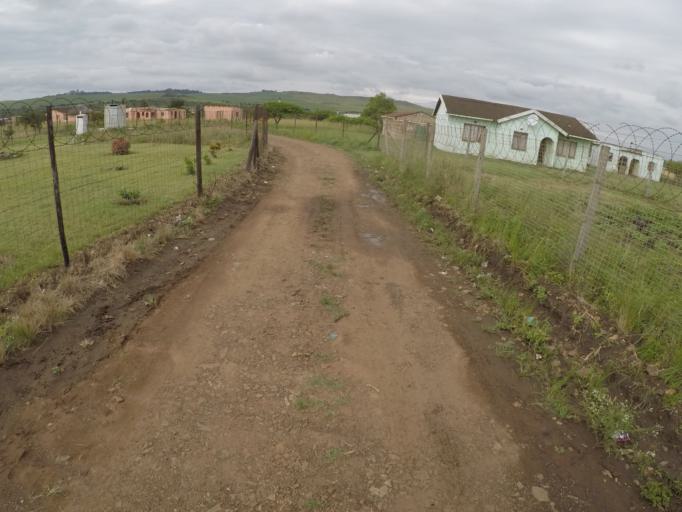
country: ZA
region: KwaZulu-Natal
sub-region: uThungulu District Municipality
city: Empangeni
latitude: -28.7132
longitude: 31.8575
